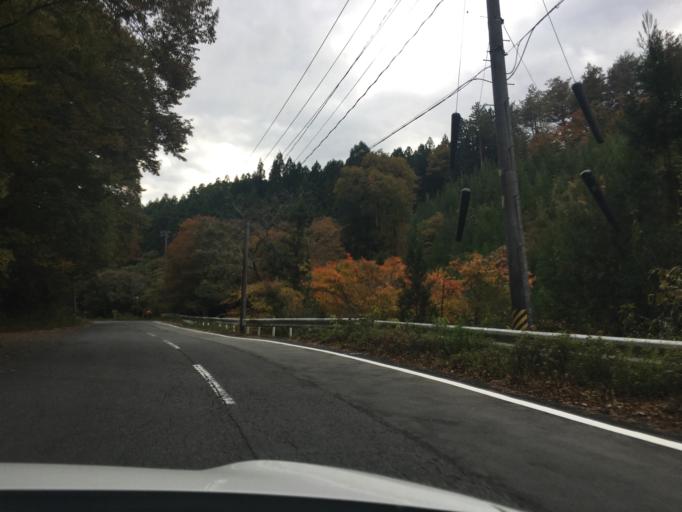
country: JP
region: Fukushima
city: Iwaki
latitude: 37.1238
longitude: 140.7753
